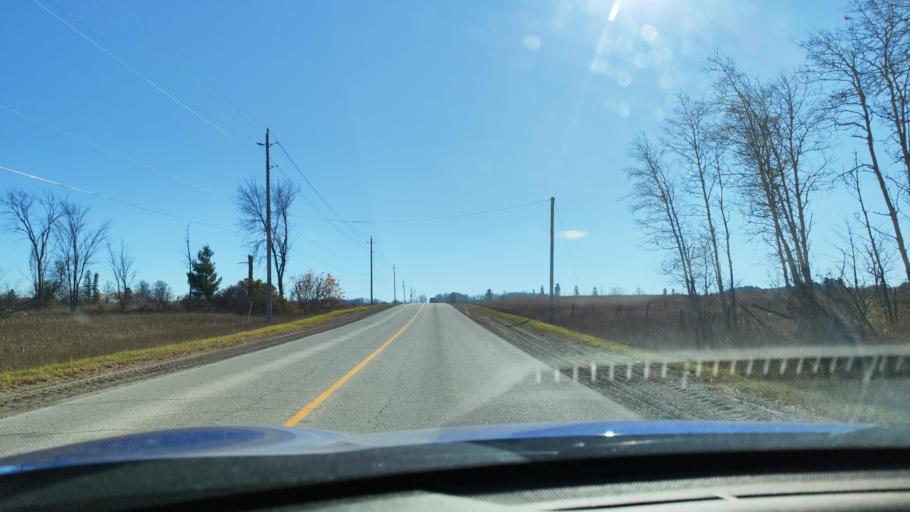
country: CA
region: Ontario
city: Wasaga Beach
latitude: 44.4630
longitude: -80.0041
